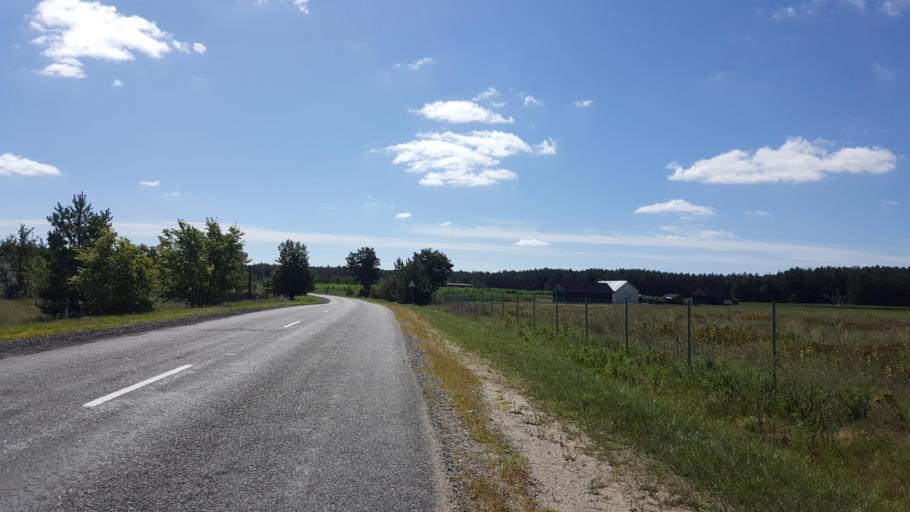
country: BY
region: Brest
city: Zhabinka
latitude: 52.3921
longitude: 24.0966
